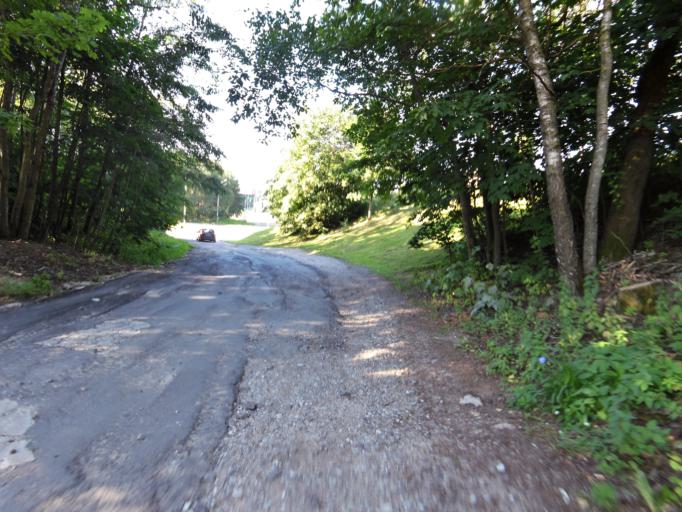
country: LT
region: Vilnius County
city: Lazdynai
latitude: 54.6872
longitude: 25.2120
